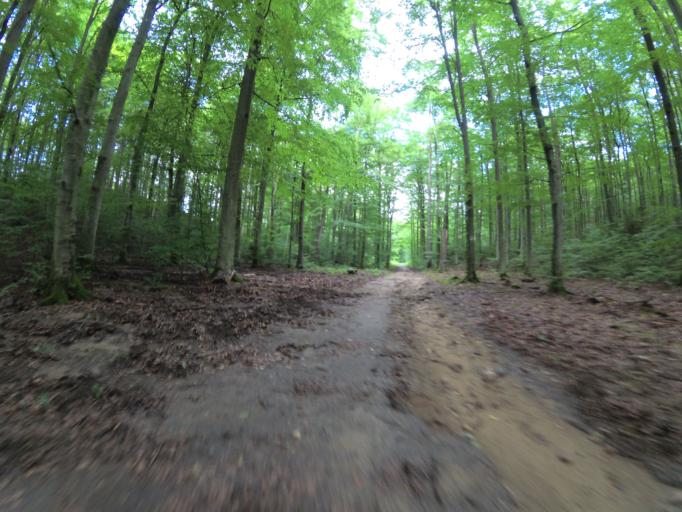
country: PL
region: Pomeranian Voivodeship
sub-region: Gdynia
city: Wielki Kack
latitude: 54.5081
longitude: 18.4442
